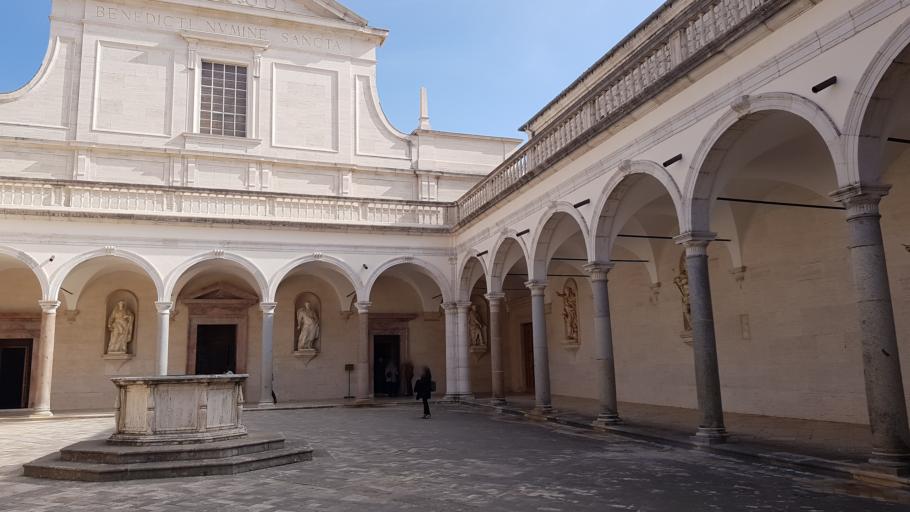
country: IT
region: Latium
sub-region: Provincia di Frosinone
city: Cassino
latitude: 41.4910
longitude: 13.8138
